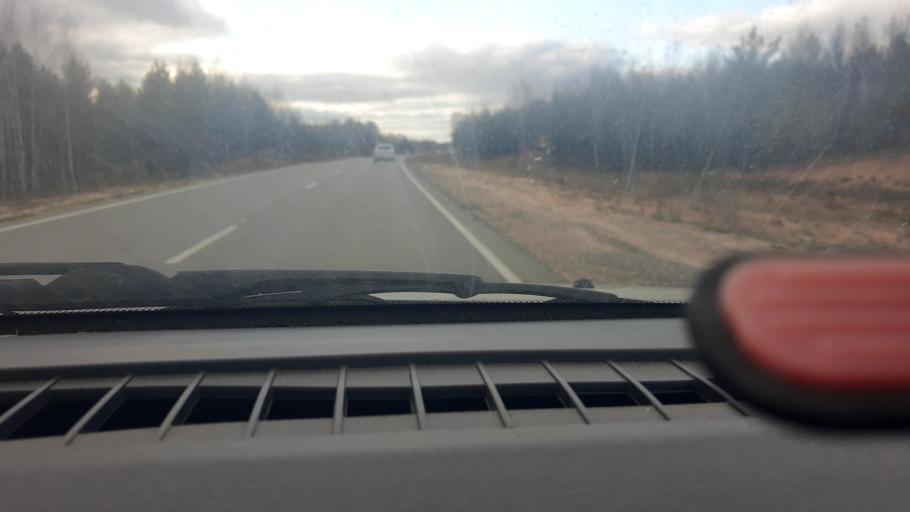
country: RU
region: Nizjnij Novgorod
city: Babino
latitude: 56.2961
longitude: 43.6351
